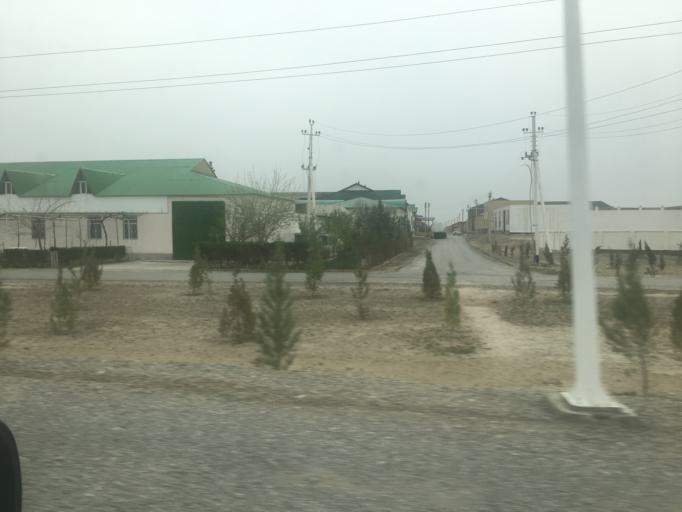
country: TM
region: Lebap
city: Turkmenabat
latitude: 38.9885
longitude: 63.5701
